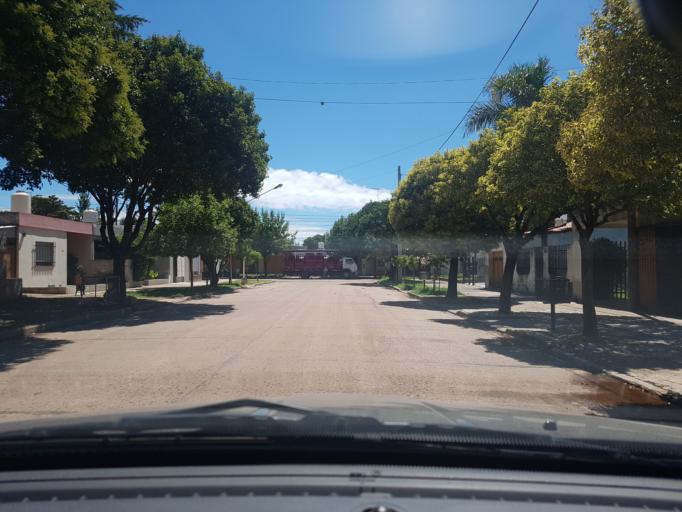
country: AR
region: Cordoba
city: General Cabrera
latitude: -32.7610
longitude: -63.7948
